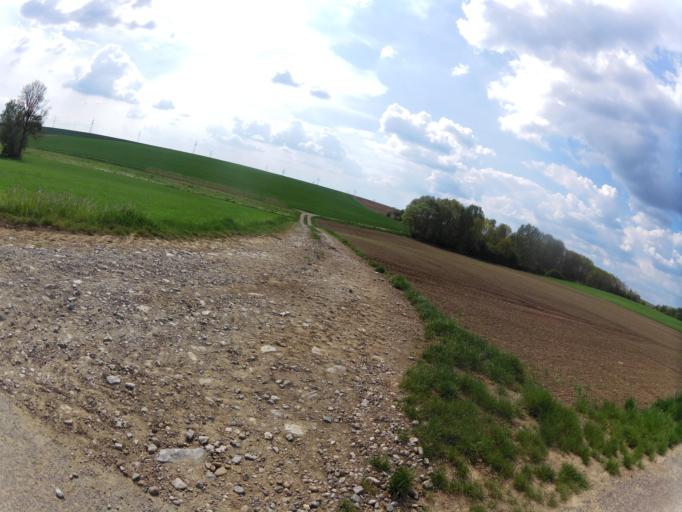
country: DE
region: Bavaria
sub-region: Regierungsbezirk Unterfranken
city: Giebelstadt
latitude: 49.6197
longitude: 9.9416
